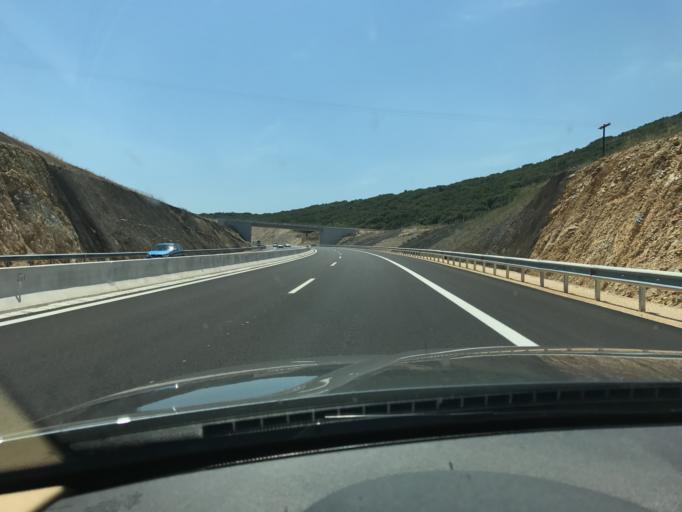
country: GR
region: Epirus
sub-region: Nomos Ioanninon
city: Agia Kyriaki
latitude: 39.4988
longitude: 20.8890
